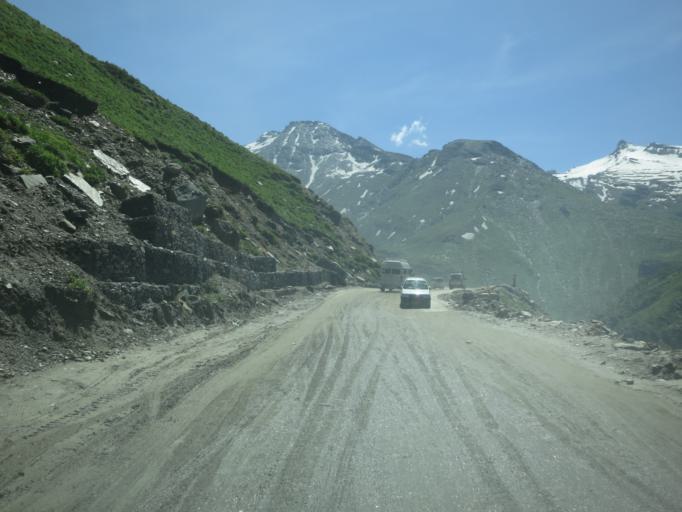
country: IN
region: Himachal Pradesh
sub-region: Kulu
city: Manali
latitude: 32.3537
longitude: 77.2174
